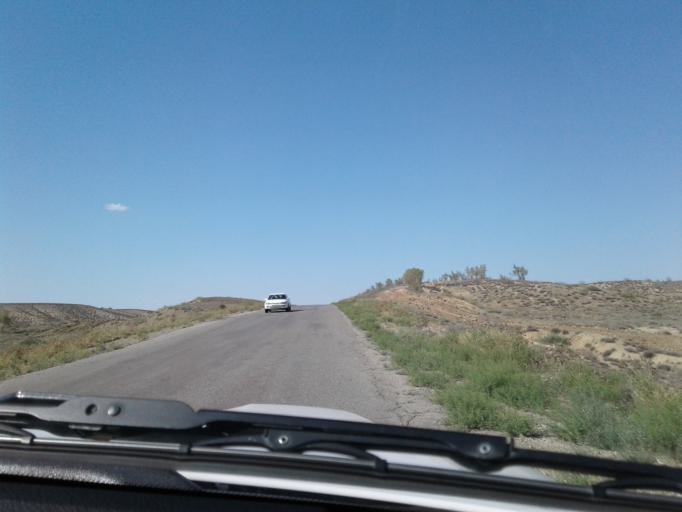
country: TM
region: Balkan
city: Magtymguly
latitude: 38.5733
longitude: 56.1859
